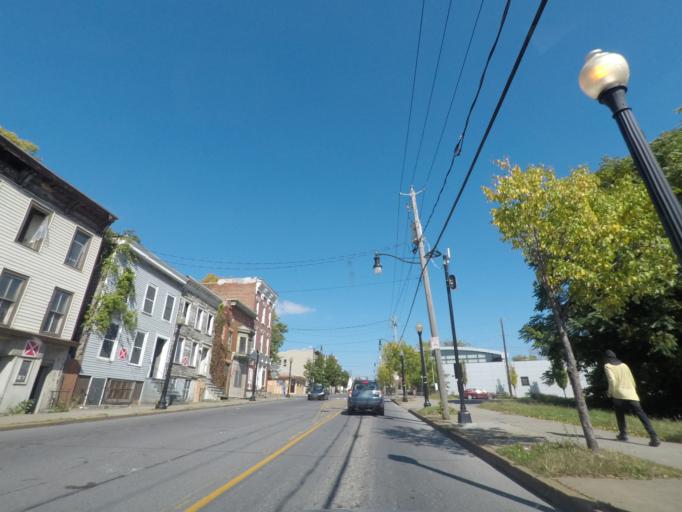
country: US
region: New York
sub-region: Albany County
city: Albany
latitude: 42.6613
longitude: -73.7612
